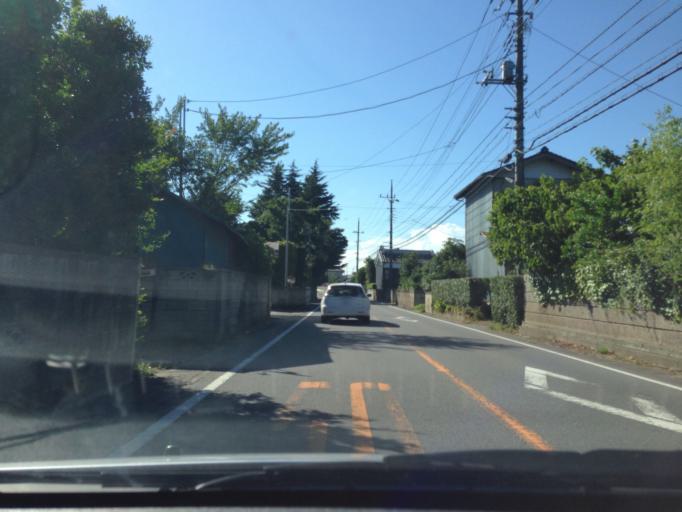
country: JP
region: Ibaraki
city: Ami
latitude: 36.0288
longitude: 140.2759
